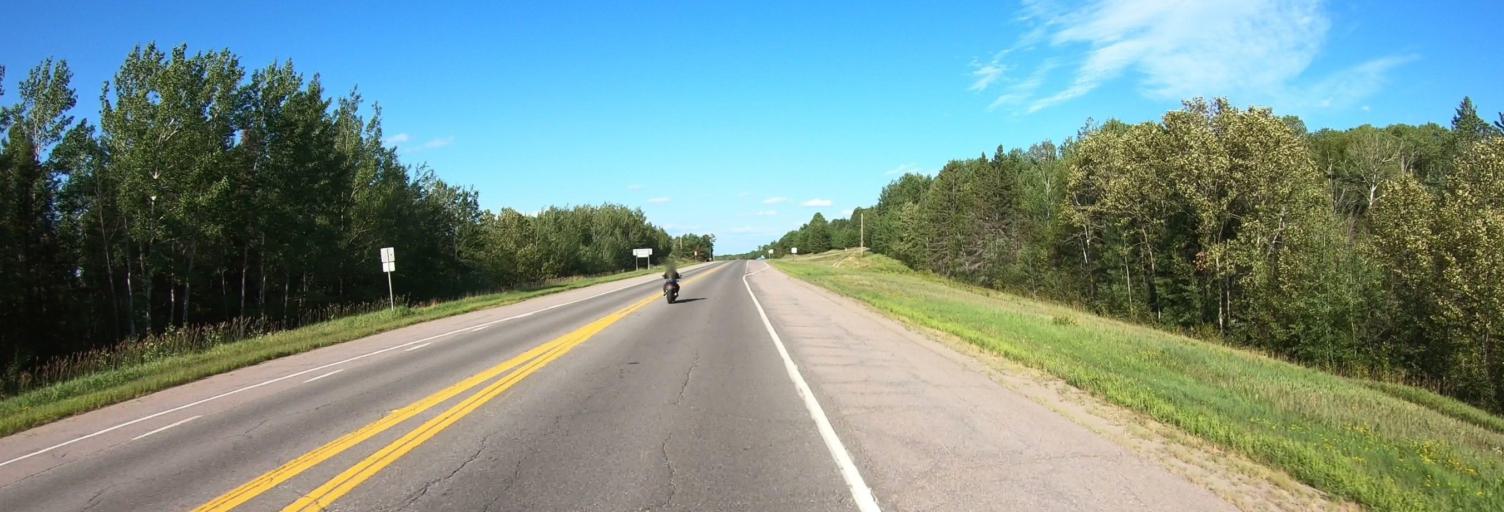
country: US
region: Minnesota
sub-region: Saint Louis County
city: Ely
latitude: 47.9093
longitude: -91.8216
